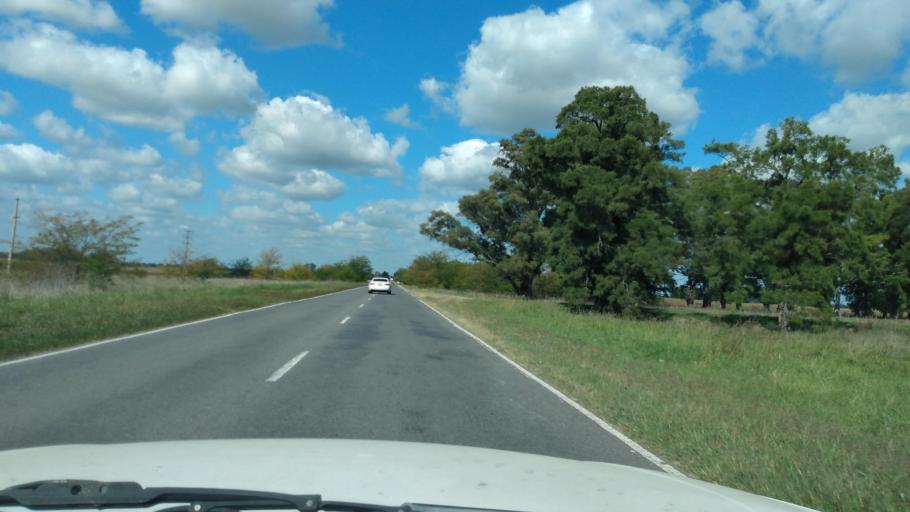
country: AR
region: Buenos Aires
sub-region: Partido de Navarro
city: Navarro
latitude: -34.9218
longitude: -59.3273
